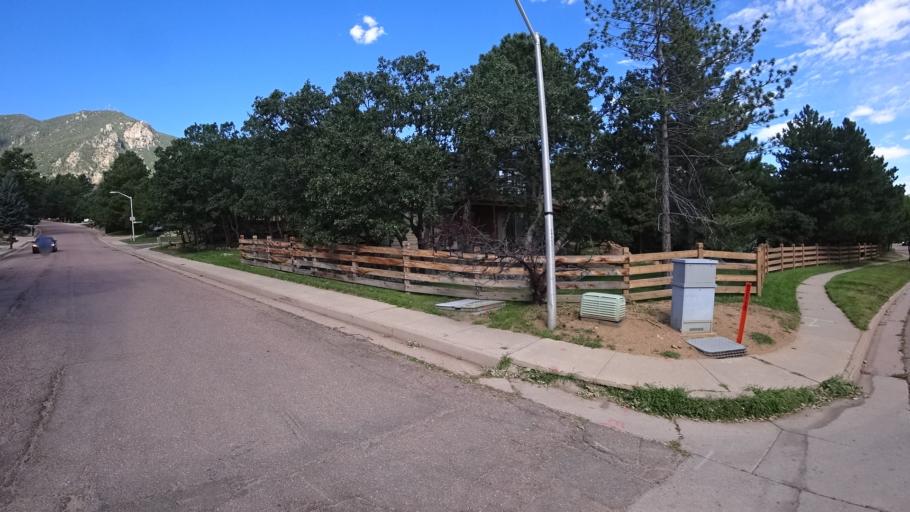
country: US
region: Colorado
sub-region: El Paso County
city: Fort Carson
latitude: 38.7573
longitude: -104.8321
